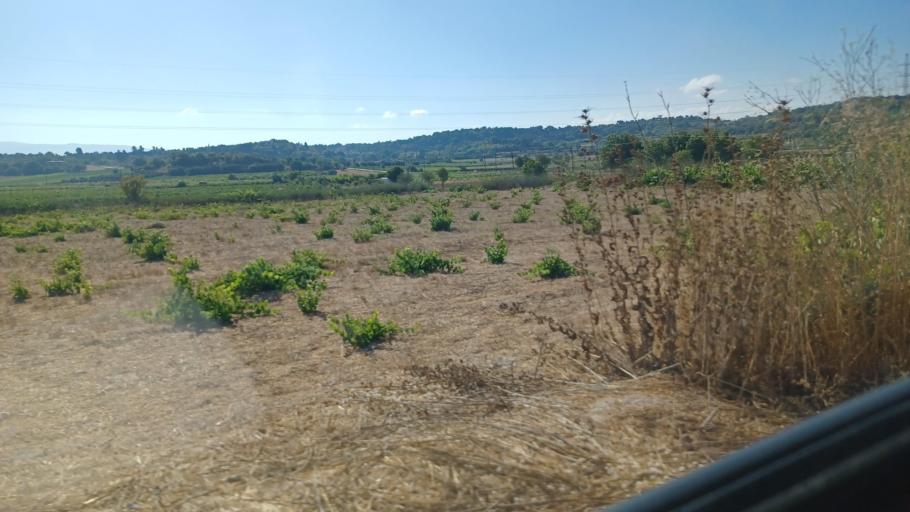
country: CY
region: Pafos
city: Tala
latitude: 34.8886
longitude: 32.4904
